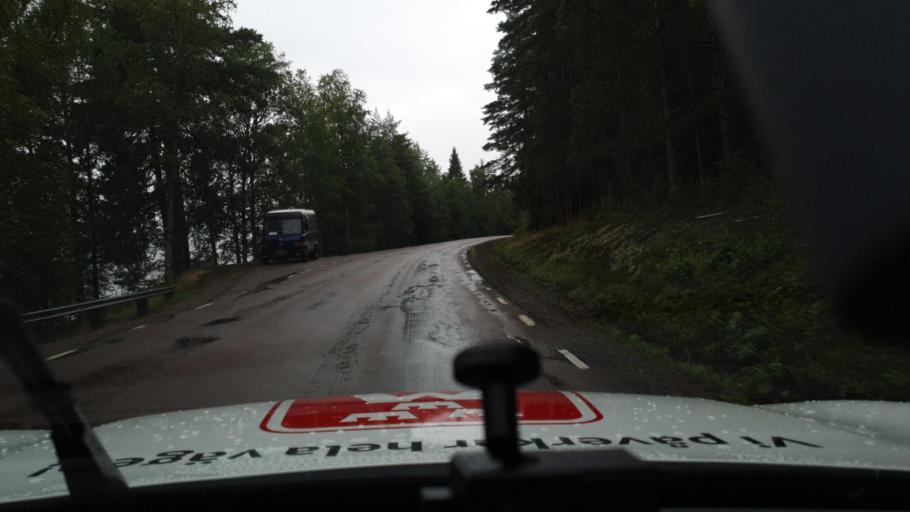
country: SE
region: Vaermland
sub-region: Arvika Kommun
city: Arvika
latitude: 59.9112
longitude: 12.6428
